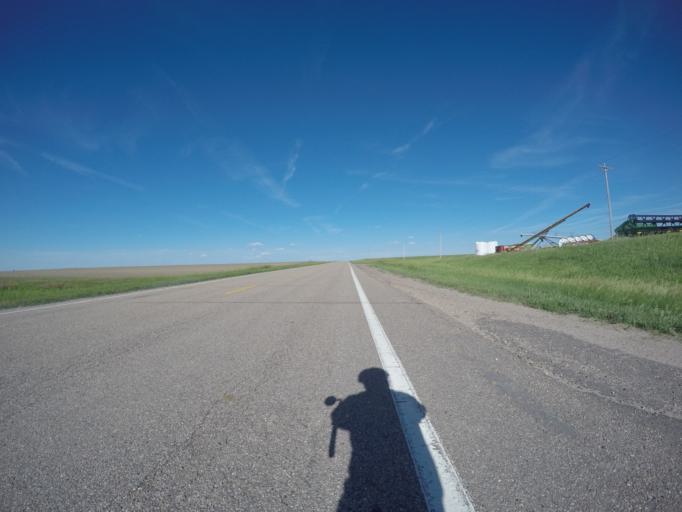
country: US
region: Kansas
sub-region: Cheyenne County
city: Saint Francis
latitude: 39.7565
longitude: -102.0122
